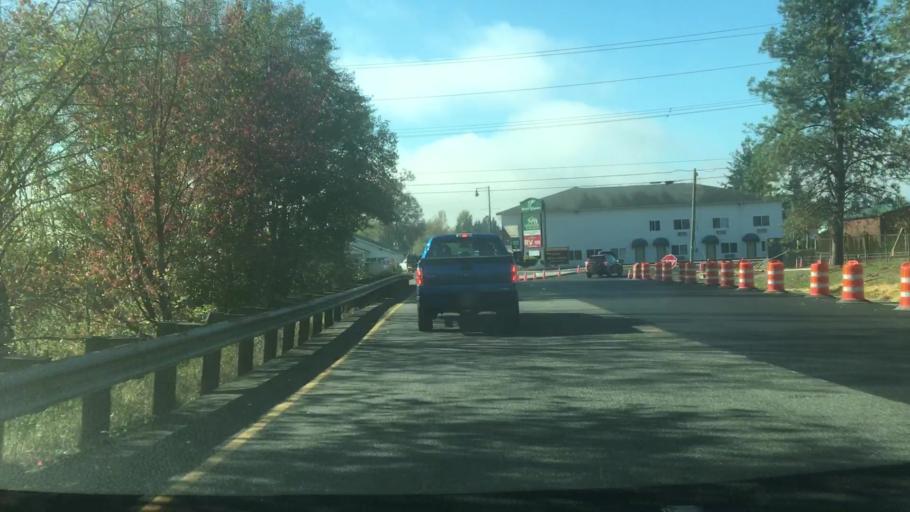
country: US
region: Washington
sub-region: Grays Harbor County
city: Montesano
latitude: 46.9770
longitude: -123.5999
